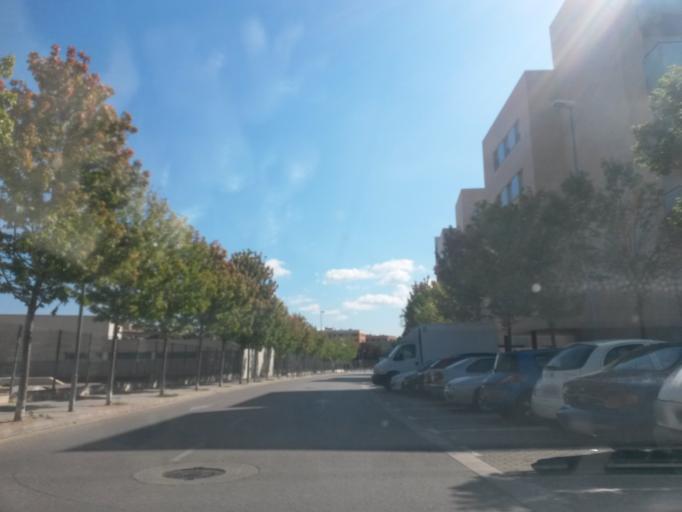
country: ES
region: Catalonia
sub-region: Provincia de Girona
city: Salt
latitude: 41.9727
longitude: 2.7991
